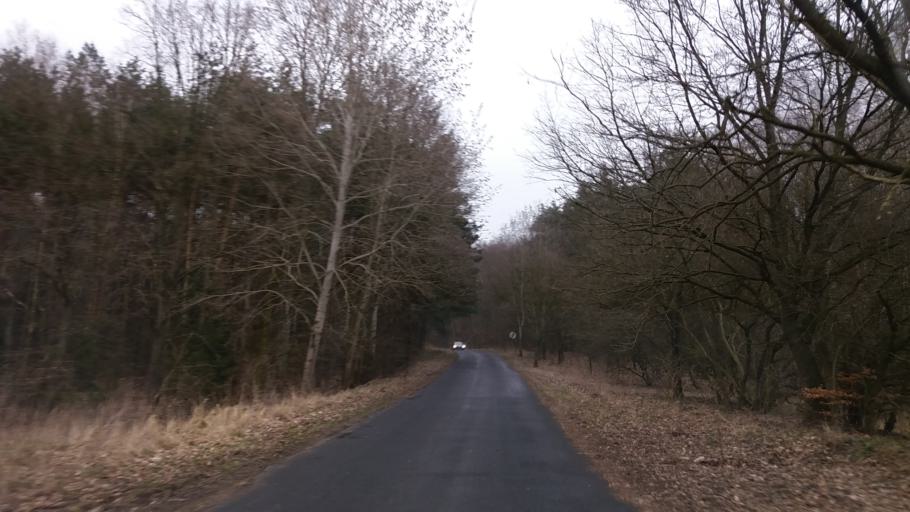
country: PL
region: West Pomeranian Voivodeship
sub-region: Powiat choszczenski
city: Choszczno
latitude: 53.2259
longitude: 15.4075
